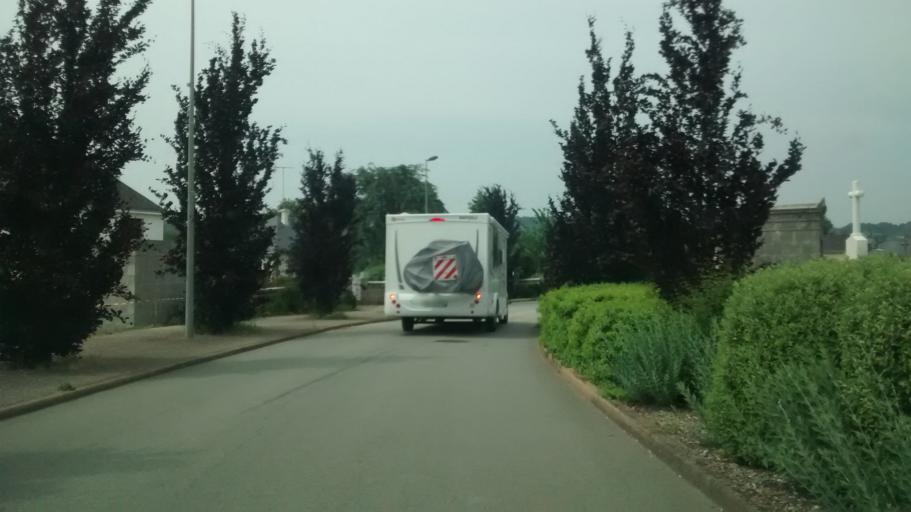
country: FR
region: Brittany
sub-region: Departement du Morbihan
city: Malestroit
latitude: 47.8119
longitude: -2.3737
